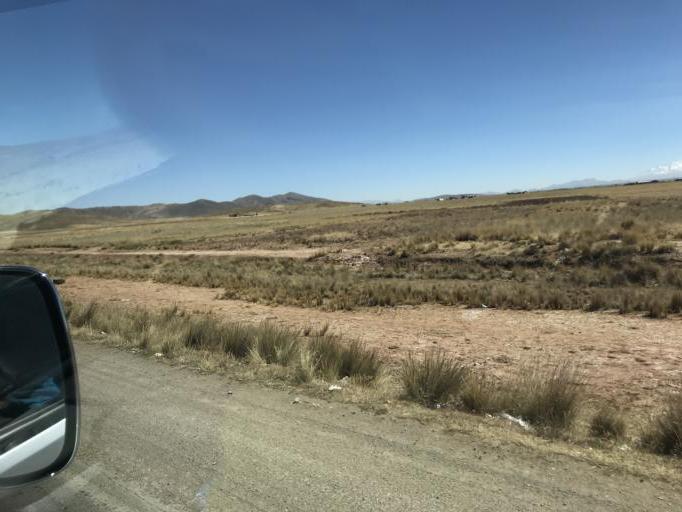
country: BO
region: La Paz
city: La Paz
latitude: -16.5312
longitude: -68.3907
